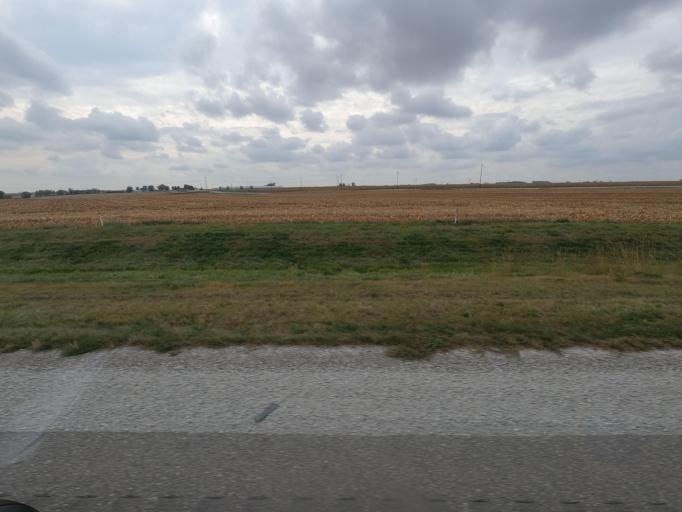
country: US
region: Iowa
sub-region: Jasper County
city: Prairie City
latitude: 41.5774
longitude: -93.1769
